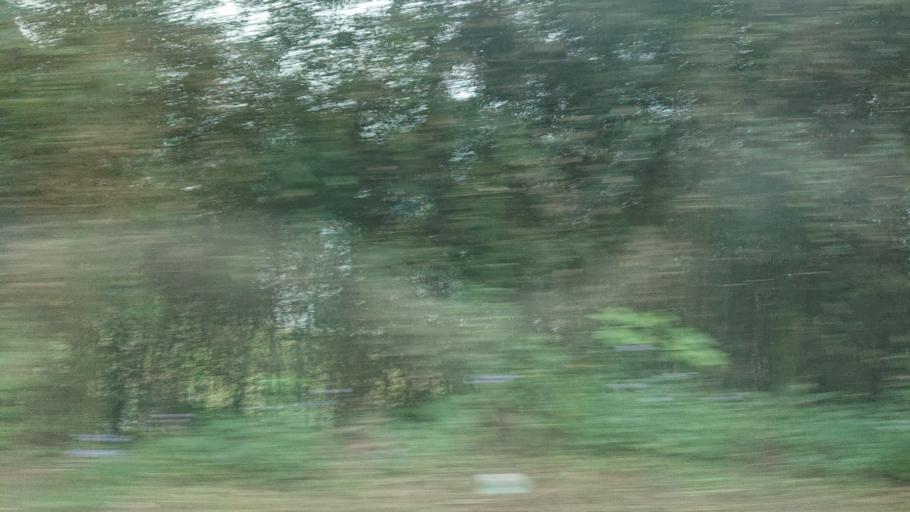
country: TW
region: Taiwan
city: Lugu
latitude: 23.6031
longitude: 120.7071
